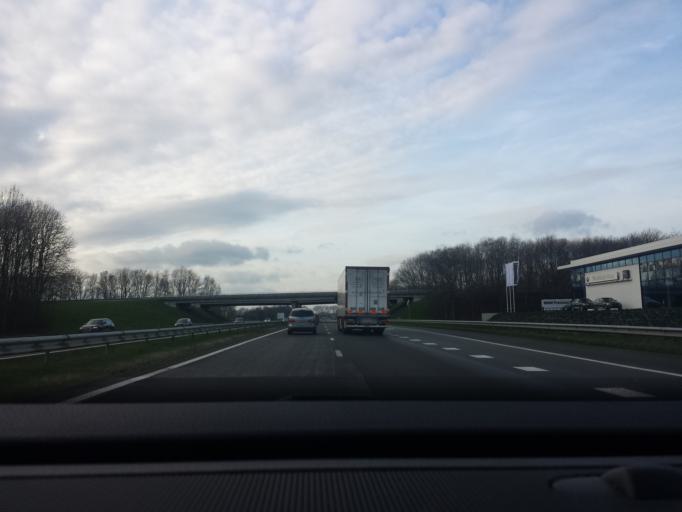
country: NL
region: Gelderland
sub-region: Gemeente Doetinchem
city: Doetinchem
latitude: 51.9437
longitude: 6.2761
